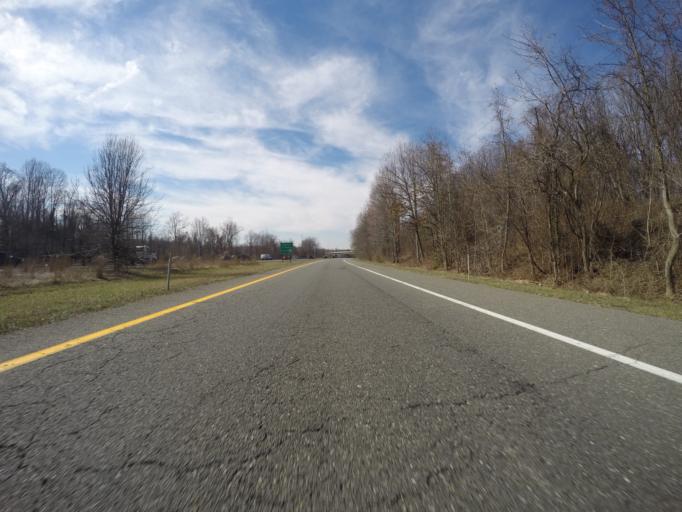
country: US
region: Maryland
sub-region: Anne Arundel County
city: Crownsville
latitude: 39.0456
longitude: -76.6175
